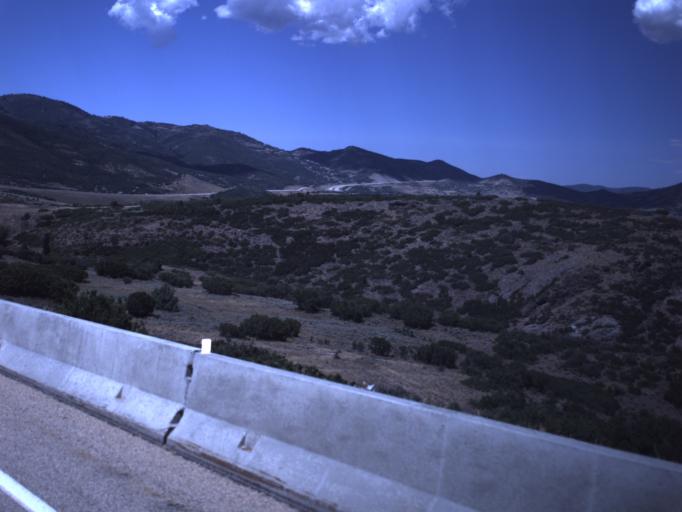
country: US
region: Utah
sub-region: Wasatch County
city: Heber
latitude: 40.5932
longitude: -111.3964
